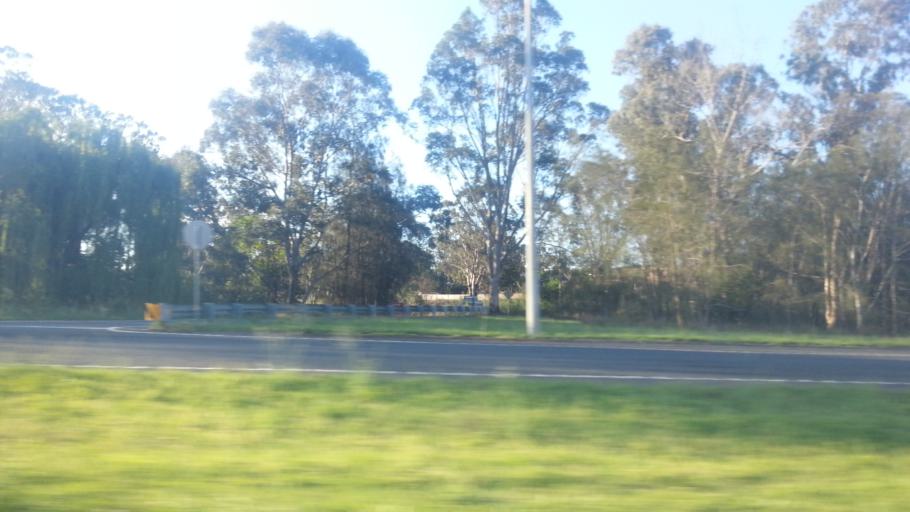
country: AU
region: New South Wales
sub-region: Camden
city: Elderslie
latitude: -34.0652
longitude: 150.7142
